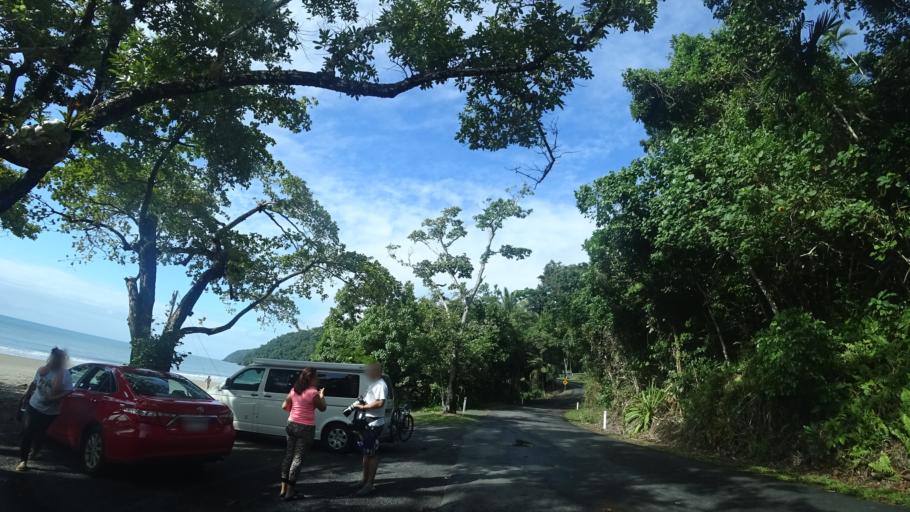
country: AU
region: Queensland
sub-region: Cassowary Coast
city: Innisfail
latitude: -17.5589
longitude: 146.0898
